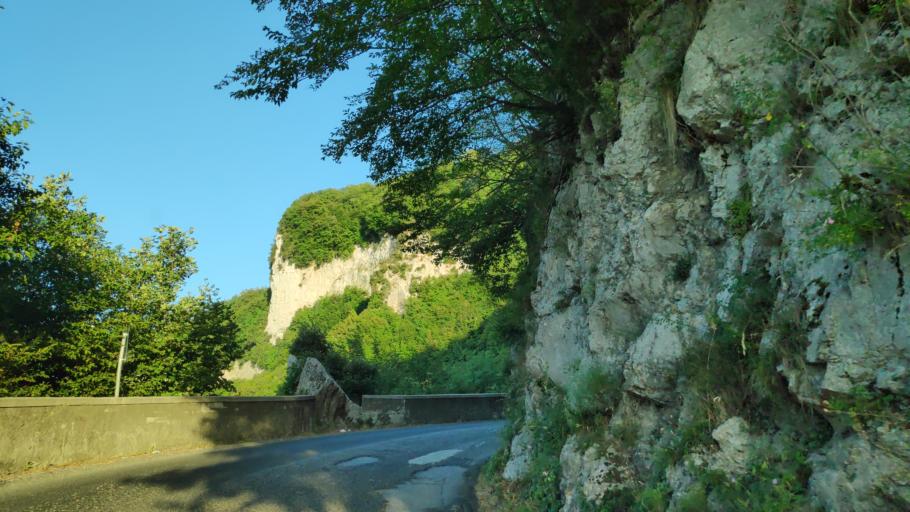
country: IT
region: Campania
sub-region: Provincia di Salerno
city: Corbara
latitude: 40.7191
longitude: 14.6109
